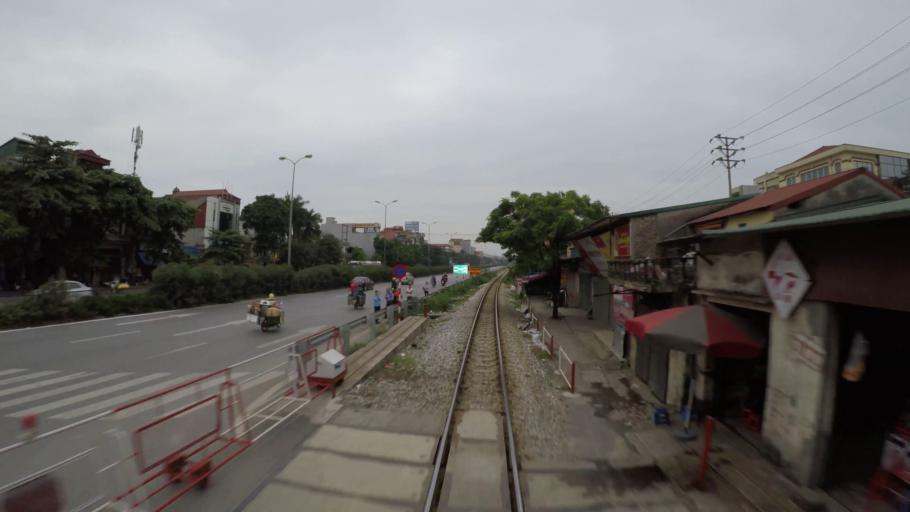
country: VN
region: Hung Yen
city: Nhu Quynh
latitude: 20.9886
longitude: 105.9761
